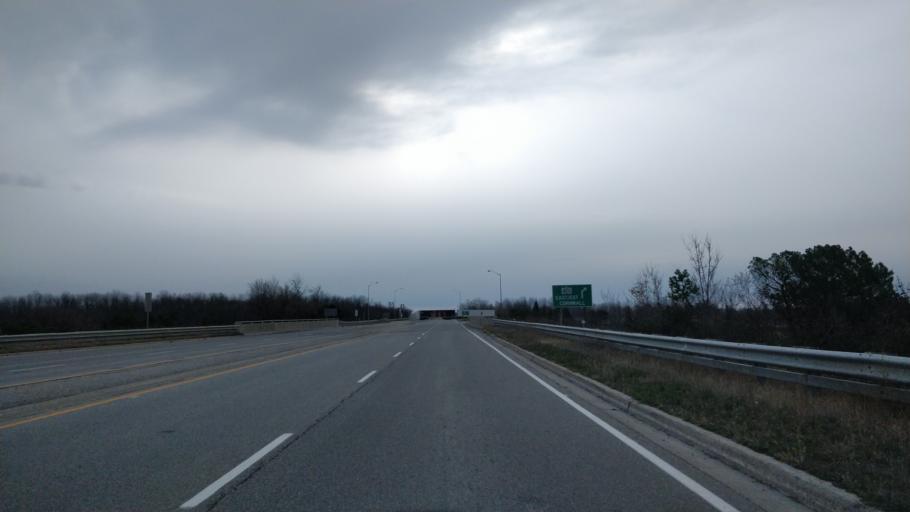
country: CA
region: Ontario
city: Prescott
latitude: 44.7553
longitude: -75.4794
